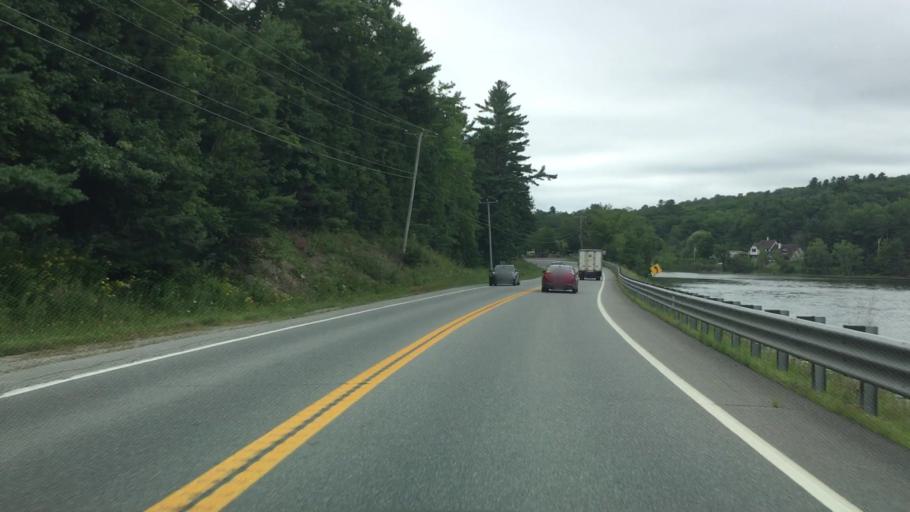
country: US
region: Maine
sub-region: Waldo County
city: Frankfort
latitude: 44.6003
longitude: -68.8678
